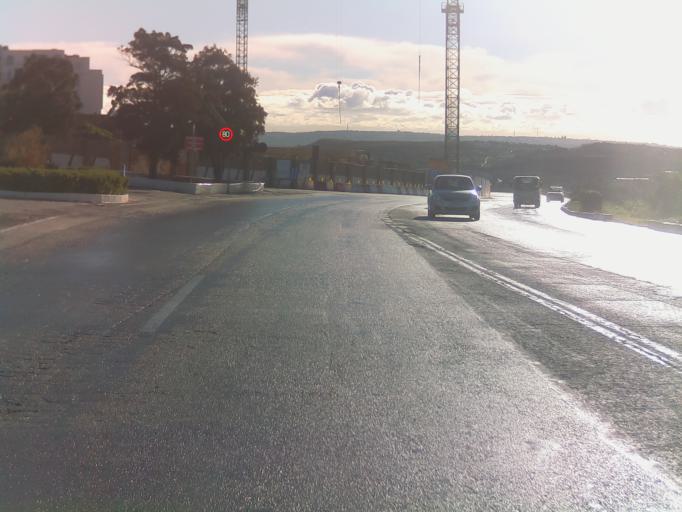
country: MT
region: Il-Mellieha
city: Mellieha
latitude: 35.9535
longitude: 14.3635
